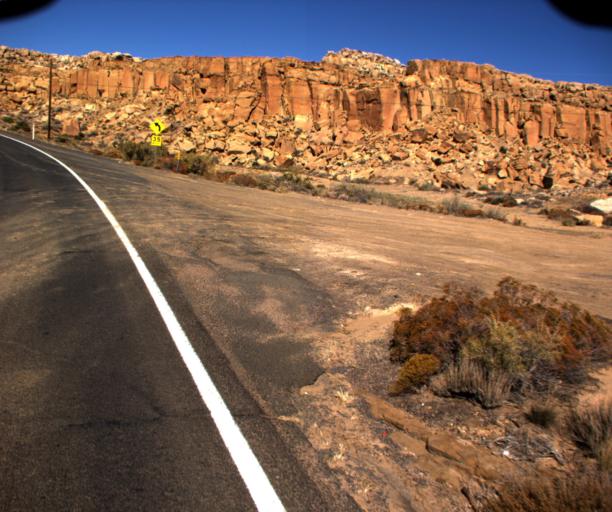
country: US
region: Arizona
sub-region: Navajo County
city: First Mesa
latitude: 35.8848
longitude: -110.6290
